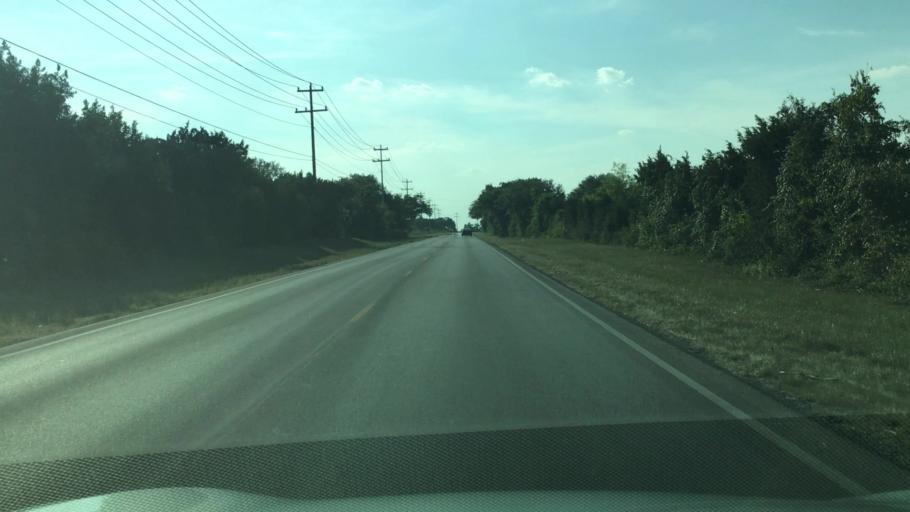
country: US
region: Texas
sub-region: Hays County
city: Buda
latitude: 30.0981
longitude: -97.9328
